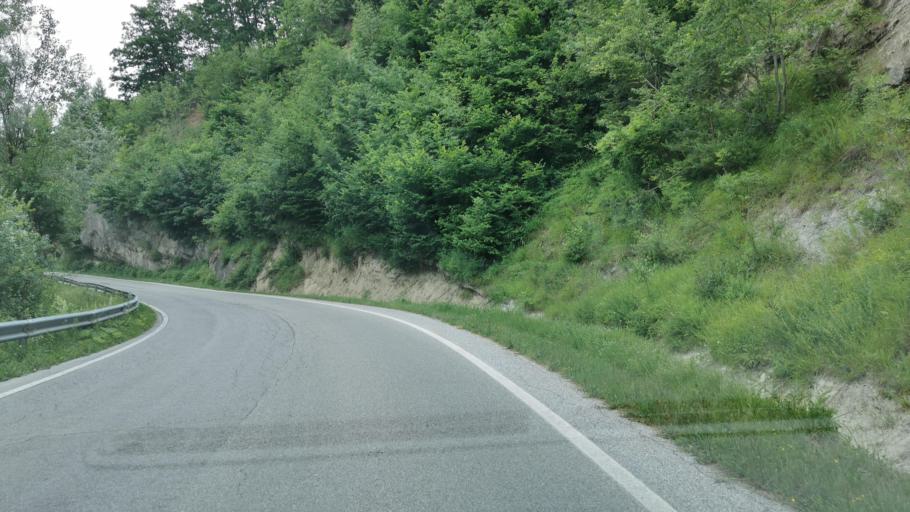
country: IT
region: Piedmont
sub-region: Provincia di Cuneo
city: Ceva
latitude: 44.4039
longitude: 8.0471
